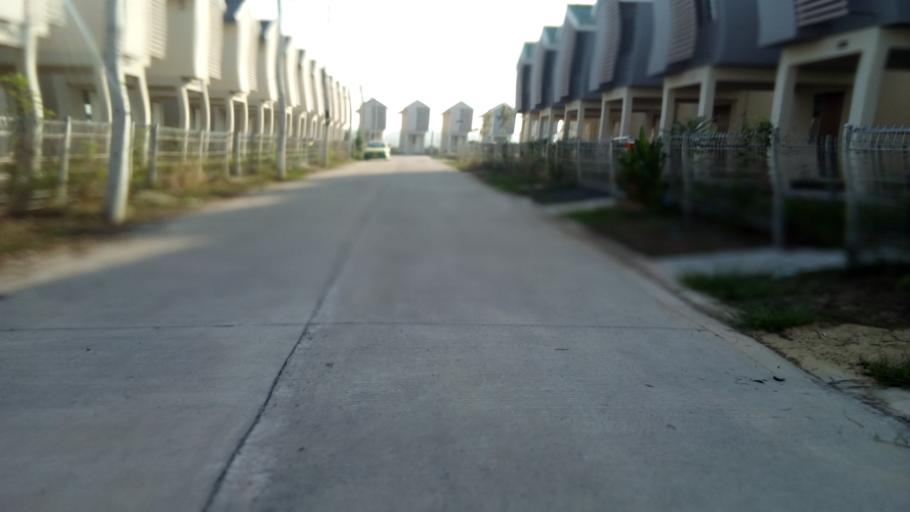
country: TH
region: Pathum Thani
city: Ban Rangsit
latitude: 14.0443
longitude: 100.8399
